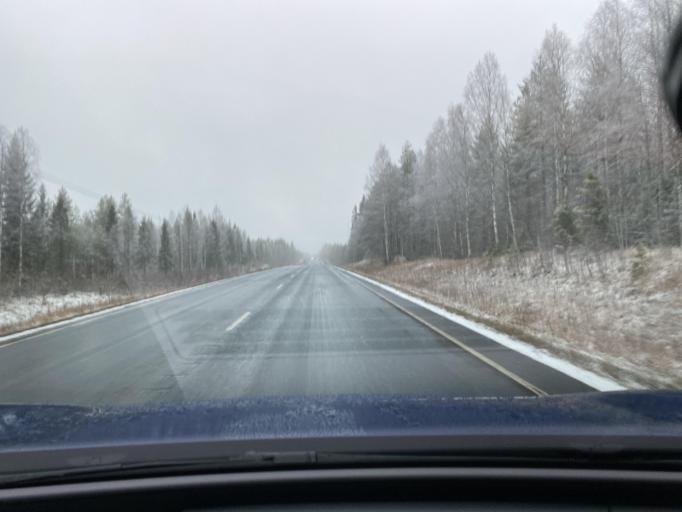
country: FI
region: Northern Ostrobothnia
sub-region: Oulu
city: Kiiminki
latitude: 65.1392
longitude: 25.8487
